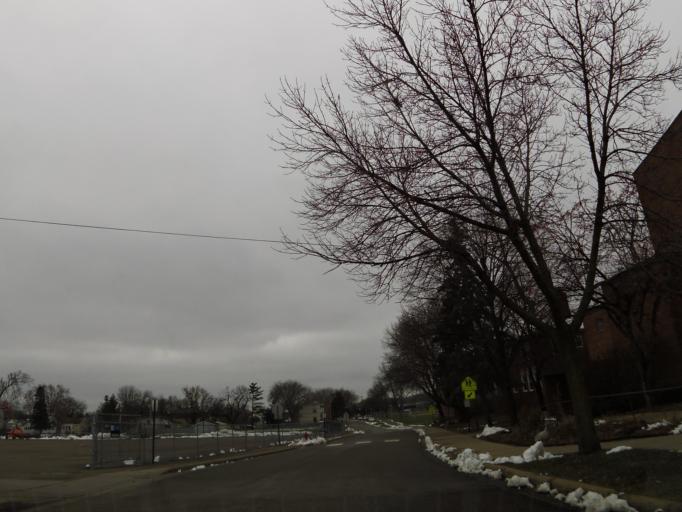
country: US
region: Minnesota
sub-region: Hennepin County
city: Minnetonka Mills
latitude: 44.9241
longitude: -93.4163
